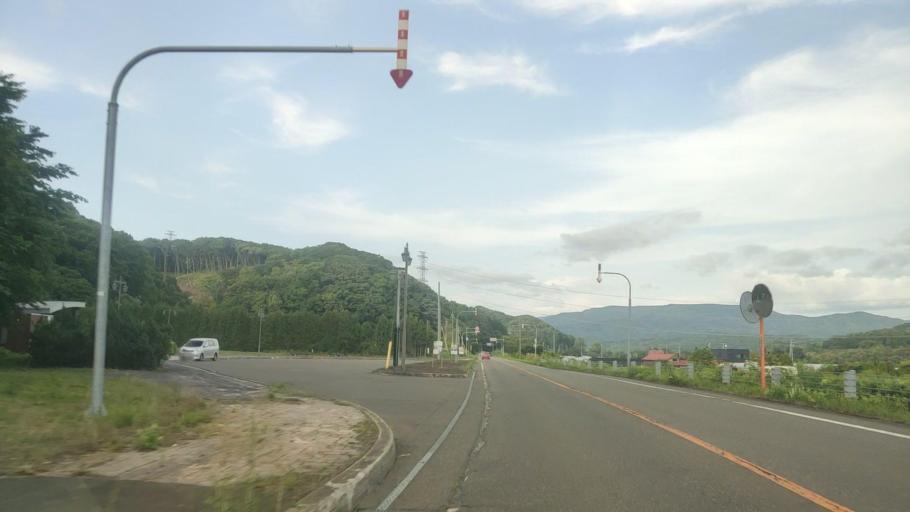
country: JP
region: Hokkaido
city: Iwamizawa
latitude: 43.0279
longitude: 141.8815
